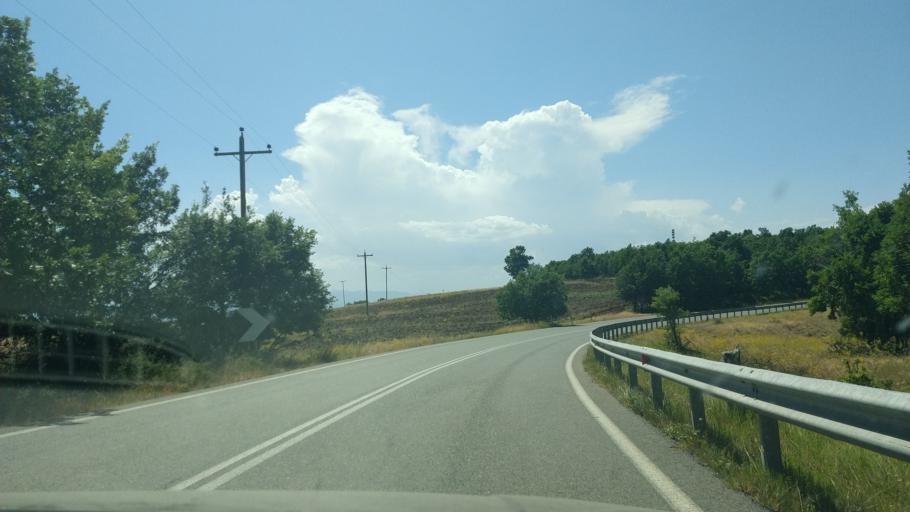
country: GR
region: West Macedonia
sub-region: Nomos Grevenon
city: Grevena
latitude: 39.9791
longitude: 21.5093
